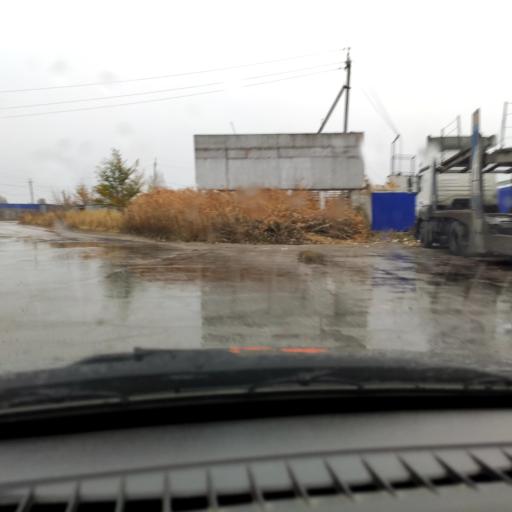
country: RU
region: Samara
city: Tol'yatti
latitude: 53.5421
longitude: 49.2887
